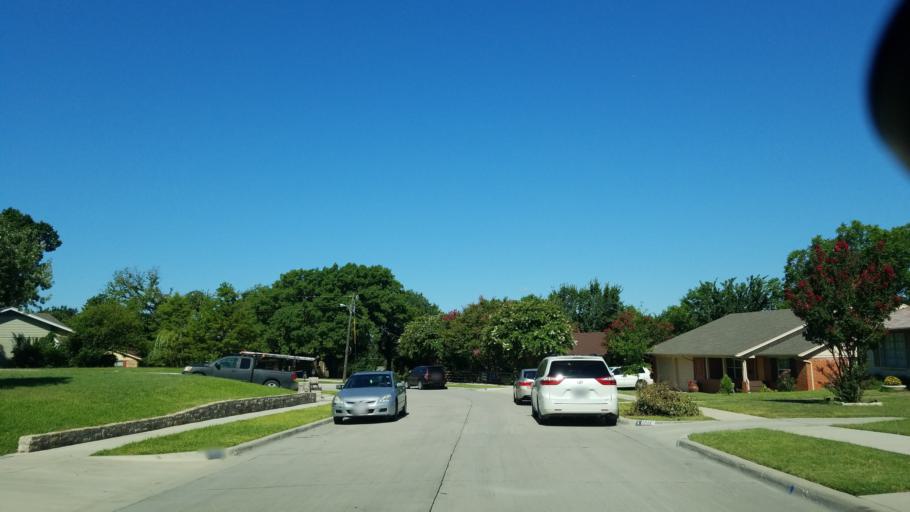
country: US
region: Texas
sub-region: Dallas County
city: Carrollton
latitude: 32.9608
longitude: -96.8943
